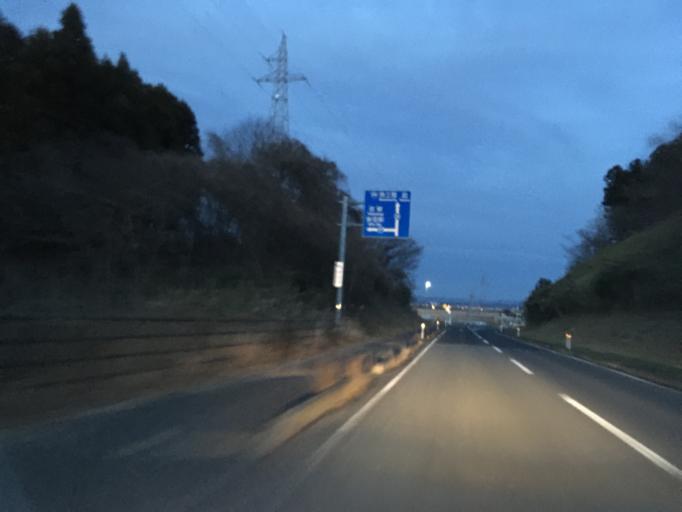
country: JP
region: Miyagi
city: Wakuya
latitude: 38.7183
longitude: 141.1350
